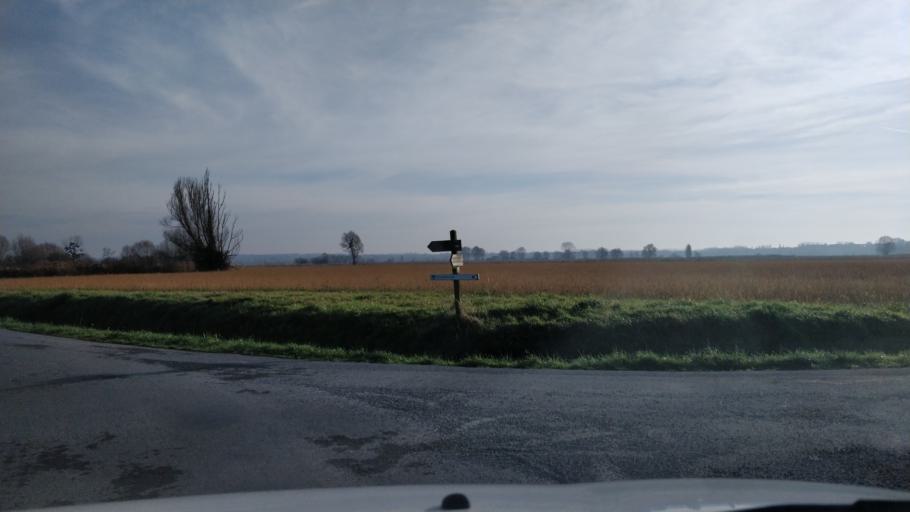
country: FR
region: Brittany
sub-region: Departement d'Ille-et-Vilaine
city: Dol-de-Bretagne
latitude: 48.5671
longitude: -1.7681
